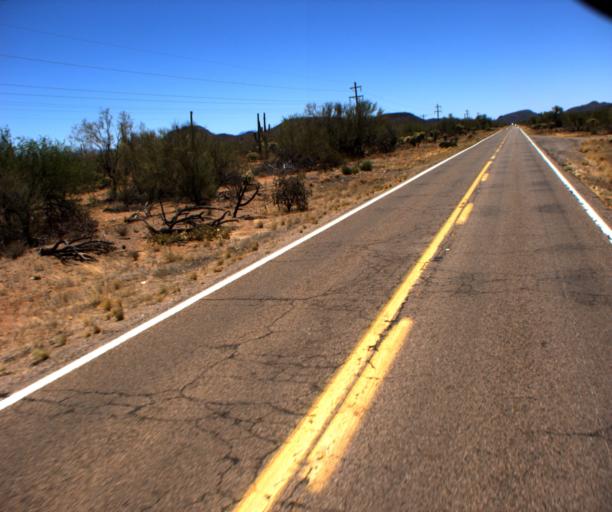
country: US
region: Arizona
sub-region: Pima County
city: Sells
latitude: 32.0040
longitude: -111.9885
